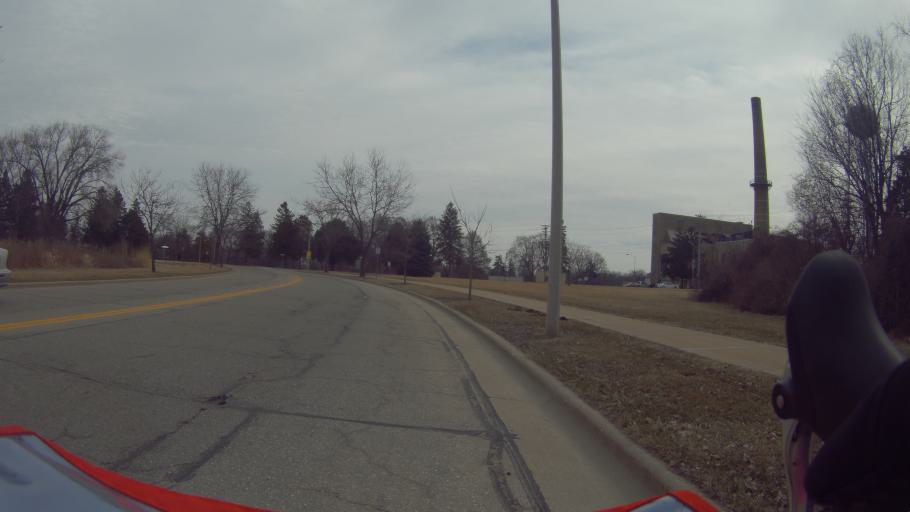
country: US
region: Wisconsin
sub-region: Dane County
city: Maple Bluff
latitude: 43.1355
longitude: -89.3978
